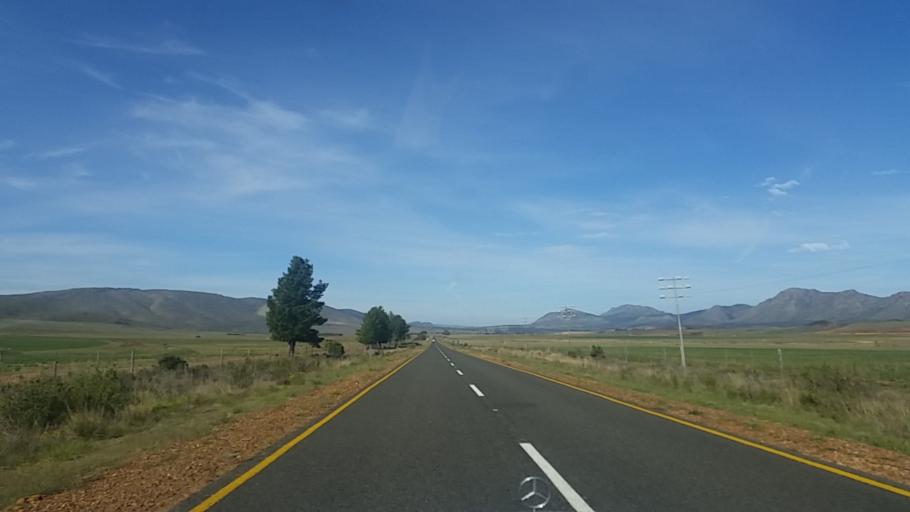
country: ZA
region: Western Cape
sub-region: Eden District Municipality
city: George
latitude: -33.8156
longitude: 22.5172
